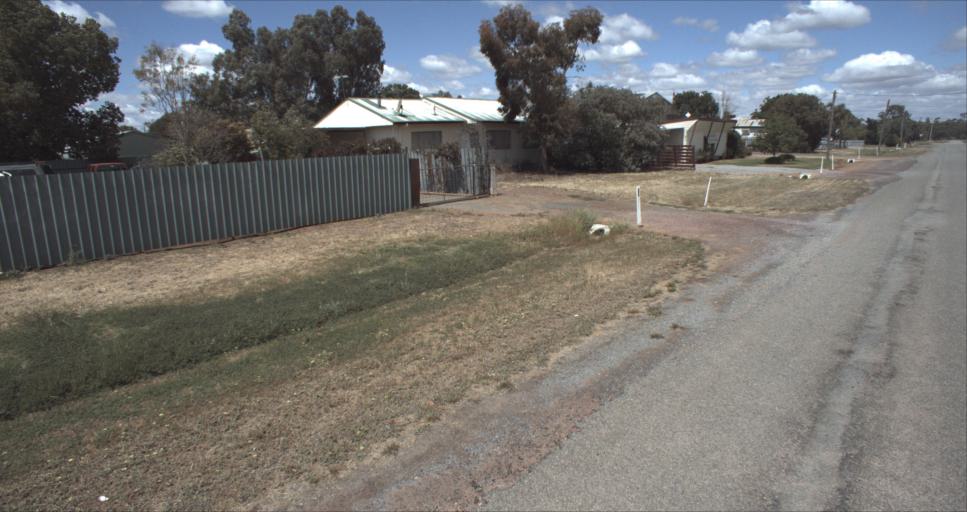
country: AU
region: New South Wales
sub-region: Murrumbidgee Shire
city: Darlington Point
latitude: -34.5182
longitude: 146.1835
